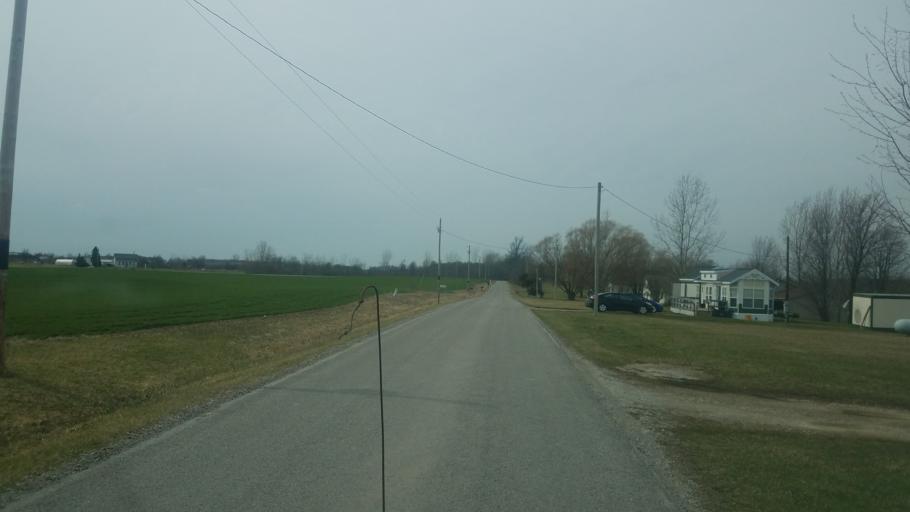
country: US
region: Ohio
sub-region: Huron County
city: Greenwich
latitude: 41.1448
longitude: -82.5269
